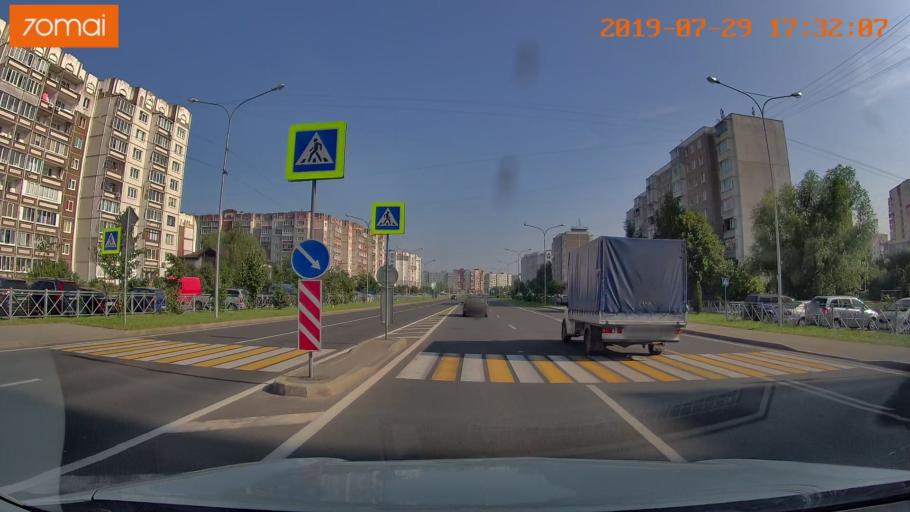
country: RU
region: Kaliningrad
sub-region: Gorod Kaliningrad
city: Kaliningrad
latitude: 54.7452
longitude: 20.4908
